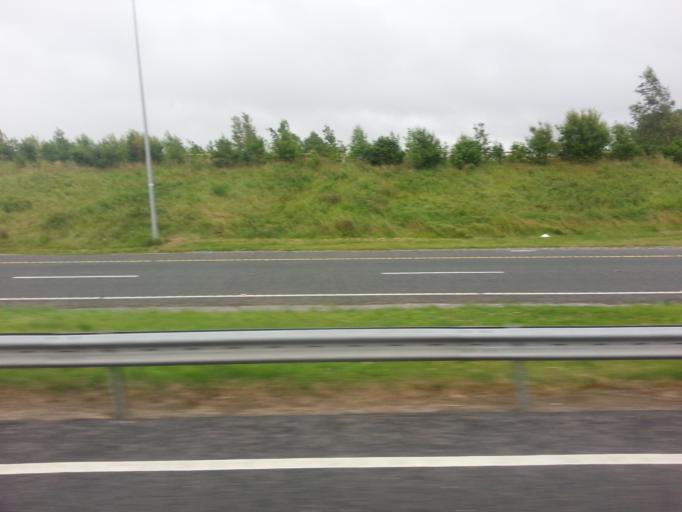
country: IE
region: Leinster
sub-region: County Carlow
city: Carlow
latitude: 52.7951
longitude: -6.8881
